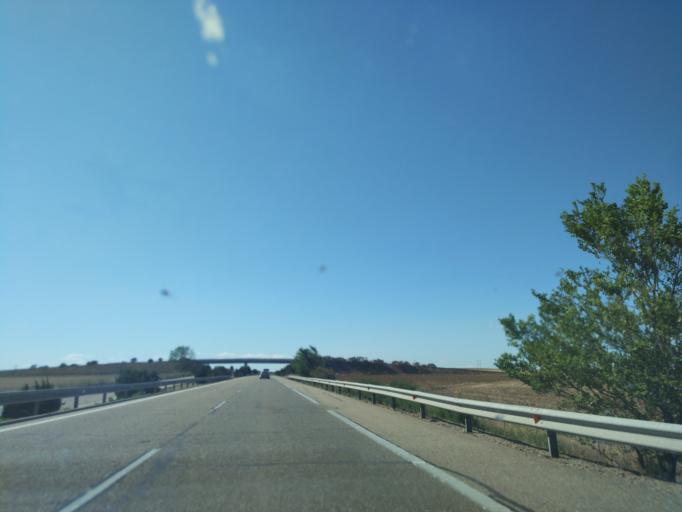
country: ES
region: Castille and Leon
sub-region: Provincia de Zamora
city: San Esteban del Molar
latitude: 41.9210
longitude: -5.5195
